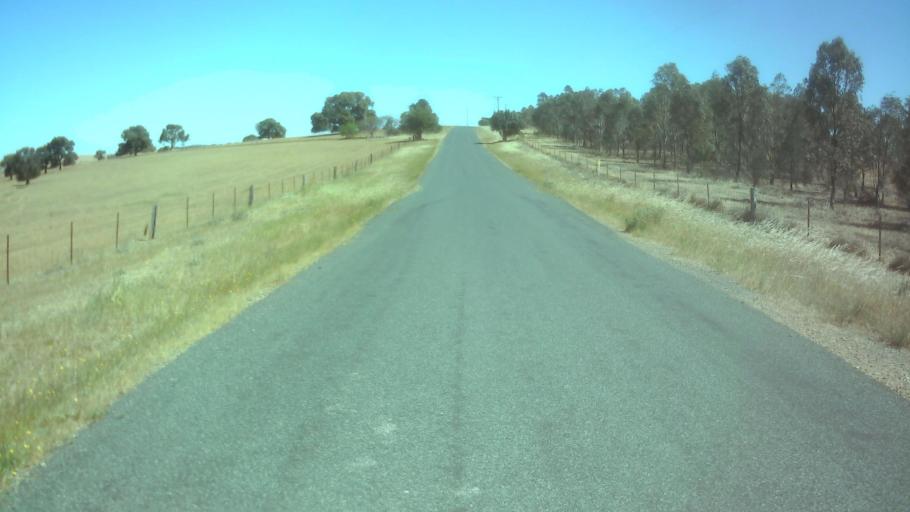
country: AU
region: New South Wales
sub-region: Weddin
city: Grenfell
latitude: -33.9605
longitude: 148.4030
